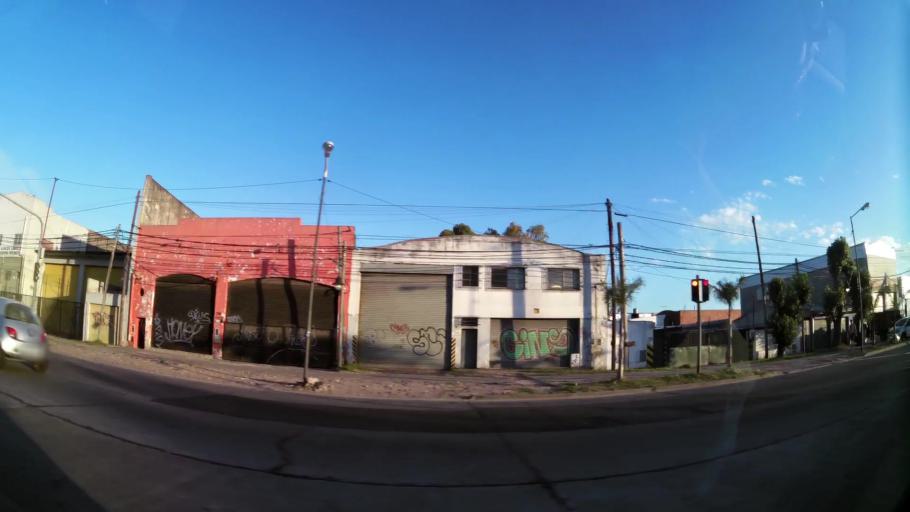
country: AR
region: Buenos Aires
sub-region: Partido de Tigre
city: Tigre
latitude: -34.4412
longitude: -58.5758
